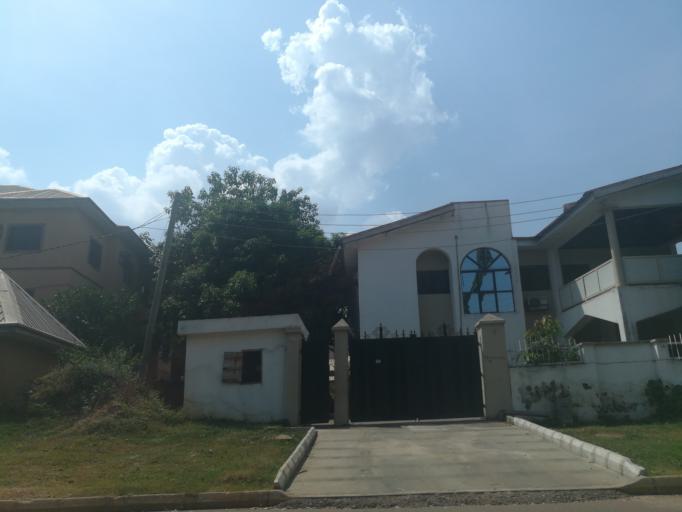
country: NG
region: Abuja Federal Capital Territory
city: Abuja
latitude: 9.0480
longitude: 7.4467
